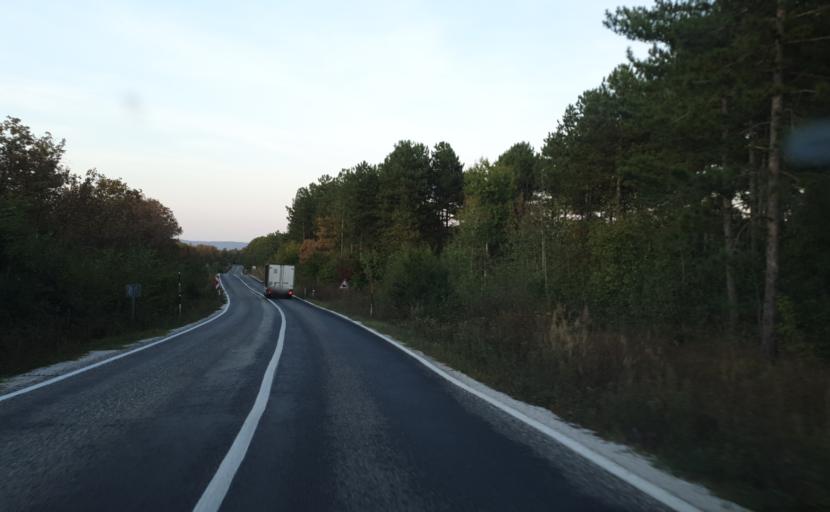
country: TR
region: Kirklareli
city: Igneada
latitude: 41.8621
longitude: 27.8825
